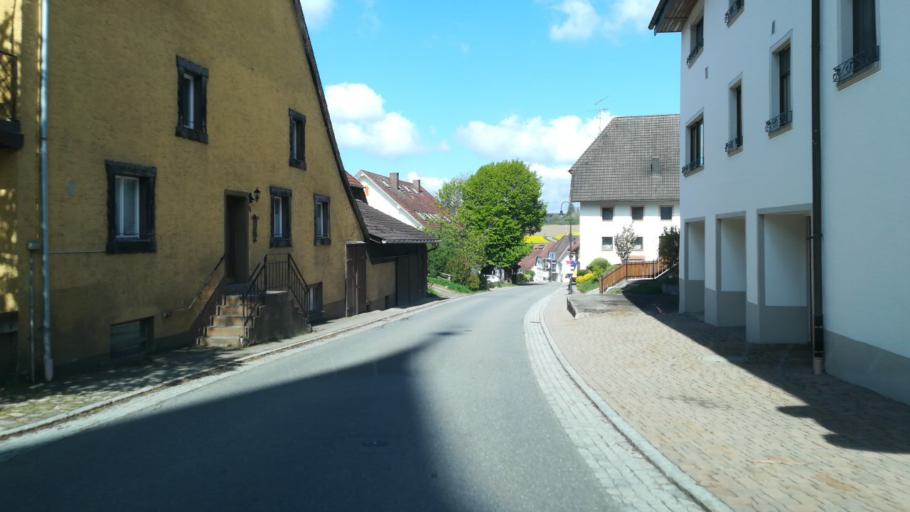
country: DE
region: Baden-Wuerttemberg
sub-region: Freiburg Region
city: Uhlingen-Birkendorf
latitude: 47.7530
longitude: 8.3644
